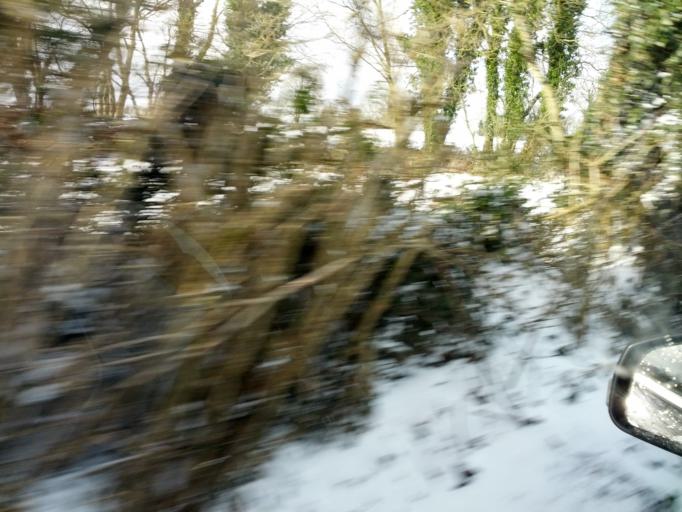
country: IE
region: Connaught
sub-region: County Galway
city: Athenry
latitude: 53.2100
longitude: -8.7569
